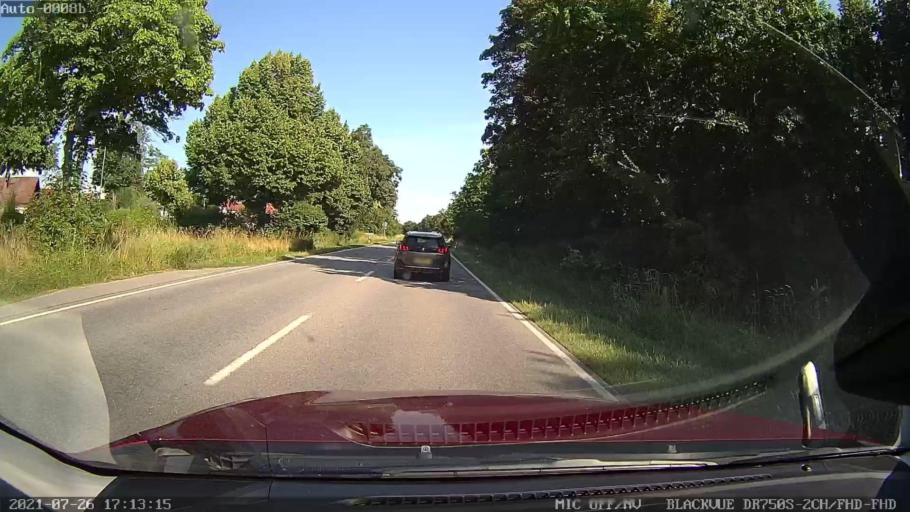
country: DE
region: Bavaria
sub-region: Upper Palatinate
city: Riekofen
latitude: 48.9713
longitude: 12.3151
